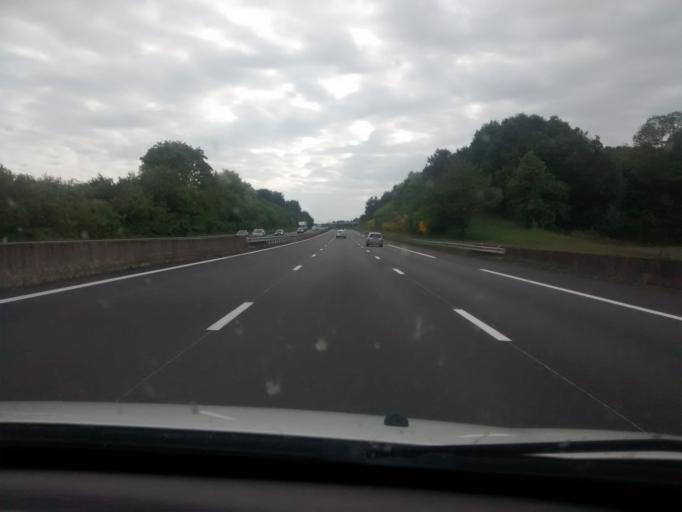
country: FR
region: Pays de la Loire
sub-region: Departement de la Sarthe
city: Tuffe
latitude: 48.0887
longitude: 0.5068
